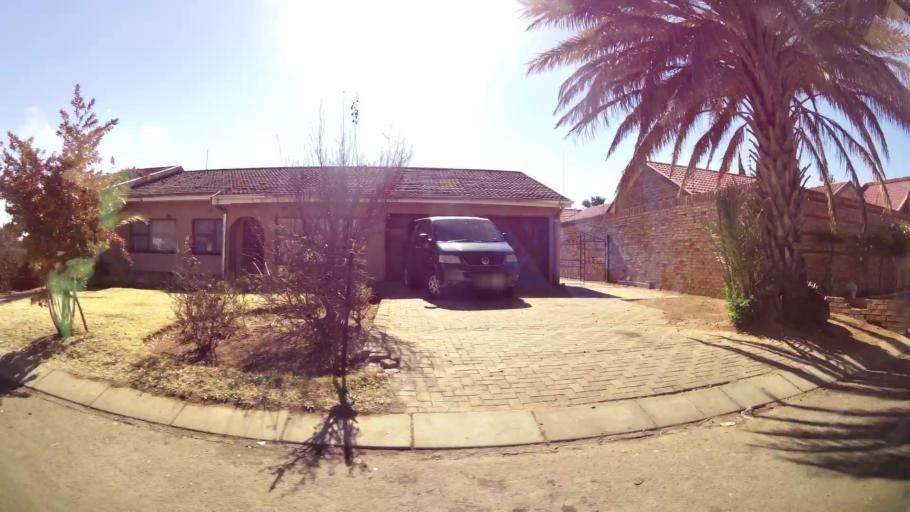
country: ZA
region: North-West
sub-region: Dr Kenneth Kaunda District Municipality
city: Klerksdorp
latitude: -26.8750
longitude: 26.5846
